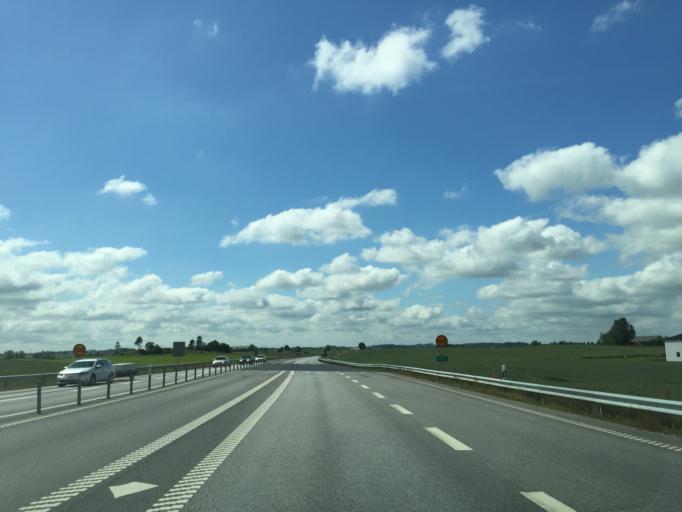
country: SE
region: Skane
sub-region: Skurups Kommun
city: Rydsgard
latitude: 55.4830
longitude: 13.5922
